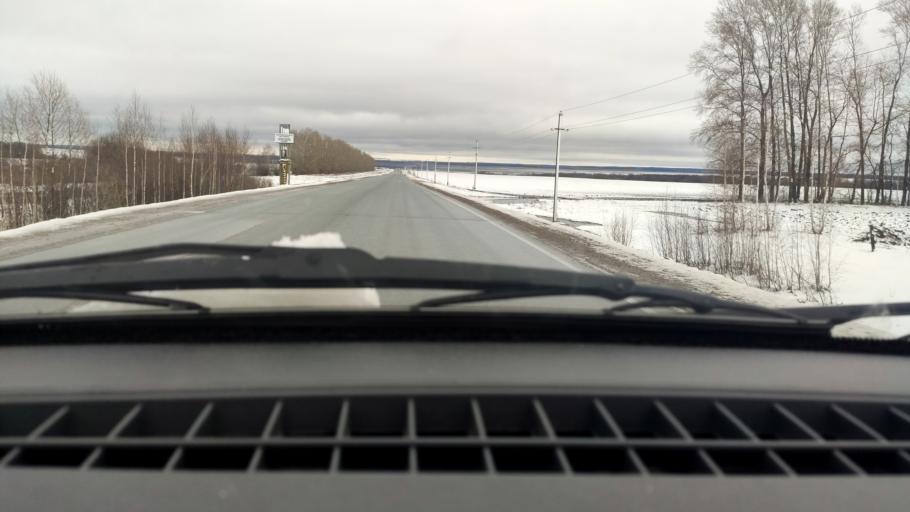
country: RU
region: Bashkortostan
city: Kushnarenkovo
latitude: 55.0601
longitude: 55.1933
